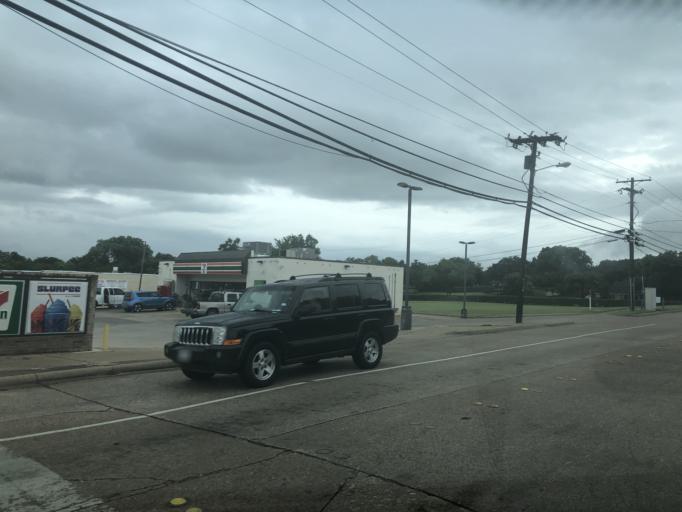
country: US
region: Texas
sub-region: Dallas County
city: Irving
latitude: 32.8012
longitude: -96.9469
